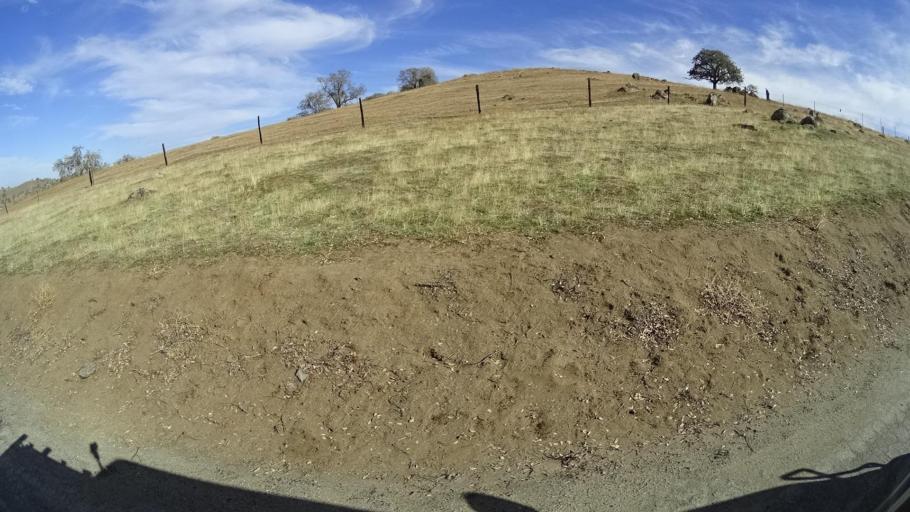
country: US
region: California
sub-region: Kern County
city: Oildale
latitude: 35.5752
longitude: -118.8100
